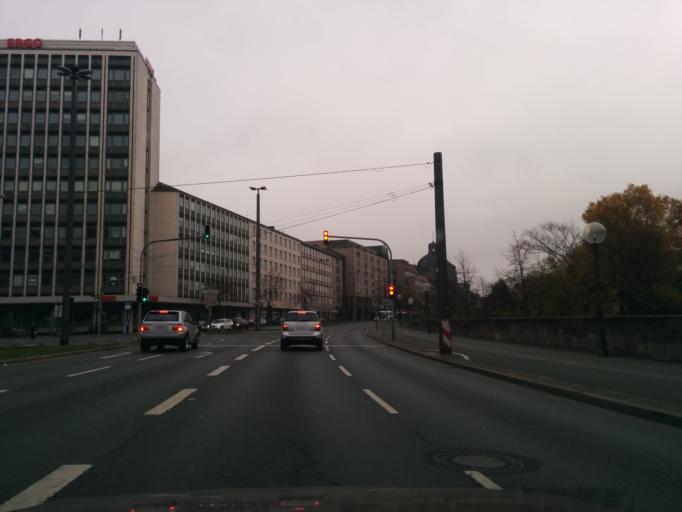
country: DE
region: Bavaria
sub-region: Regierungsbezirk Mittelfranken
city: Nuernberg
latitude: 49.4468
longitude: 11.0811
